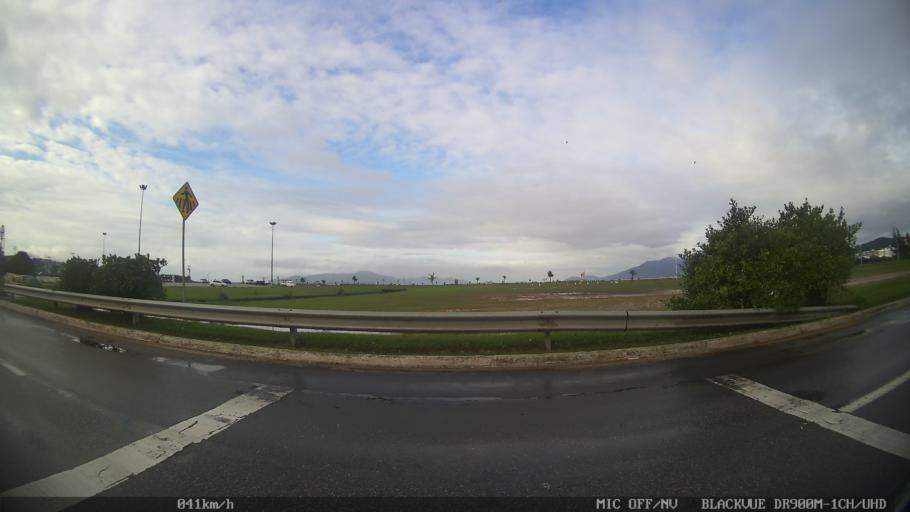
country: BR
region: Santa Catarina
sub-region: Sao Jose
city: Campinas
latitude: -27.6025
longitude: -48.6151
